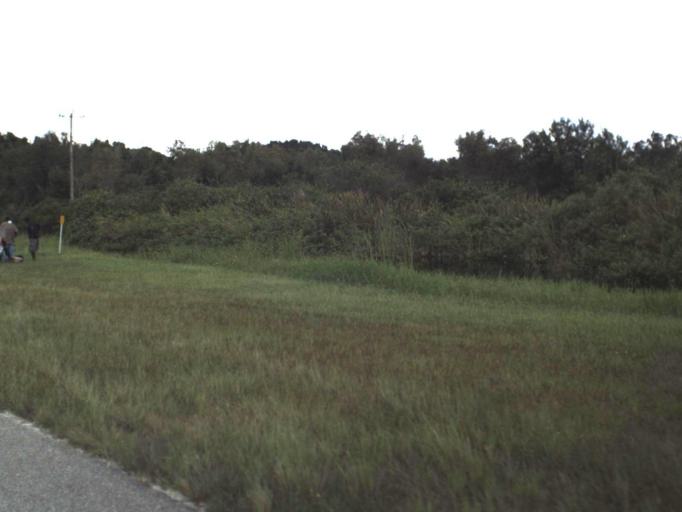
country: US
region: Florida
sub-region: Lee County
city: Suncoast Estates
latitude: 26.7893
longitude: -81.9435
